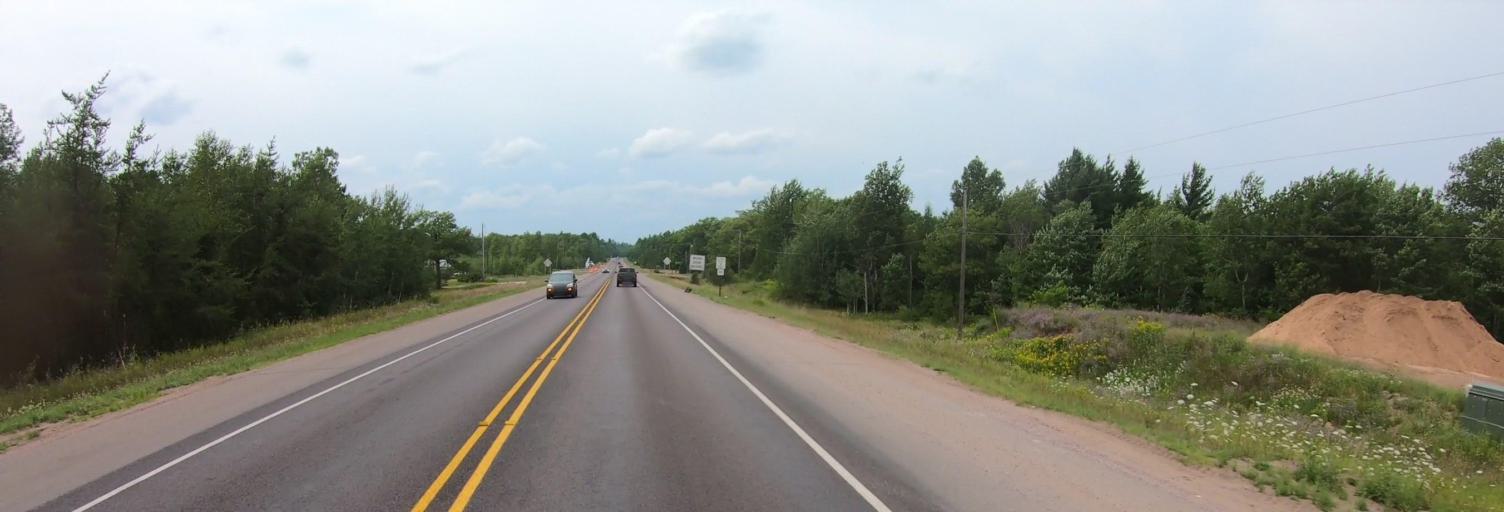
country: US
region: Michigan
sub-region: Marquette County
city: Harvey
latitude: 46.4648
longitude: -87.4269
